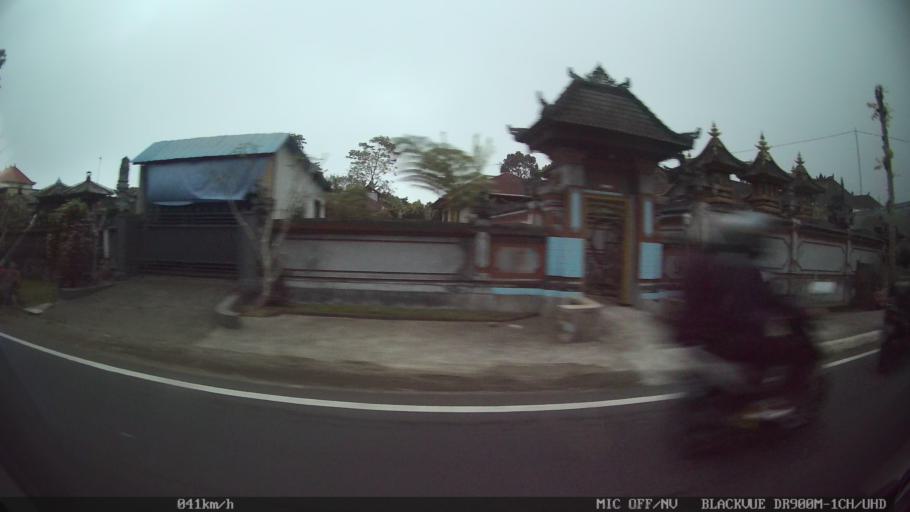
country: ID
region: Bali
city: Banjar Kedisan
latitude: -8.3014
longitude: 115.3088
